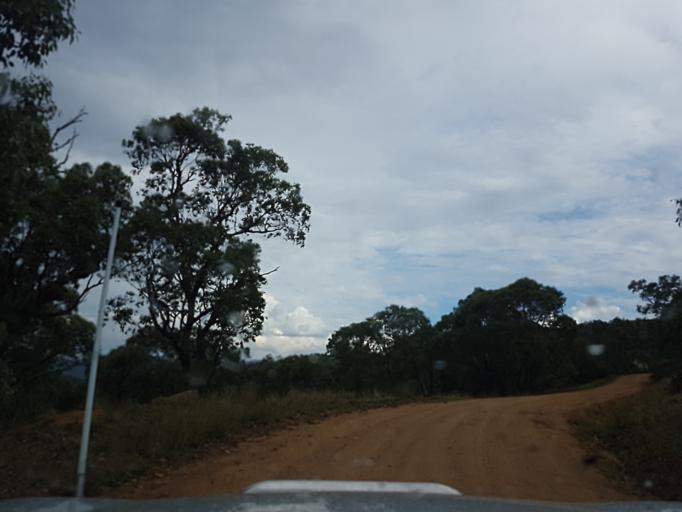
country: AU
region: New South Wales
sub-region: Snowy River
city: Jindabyne
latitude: -36.9406
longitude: 148.3459
